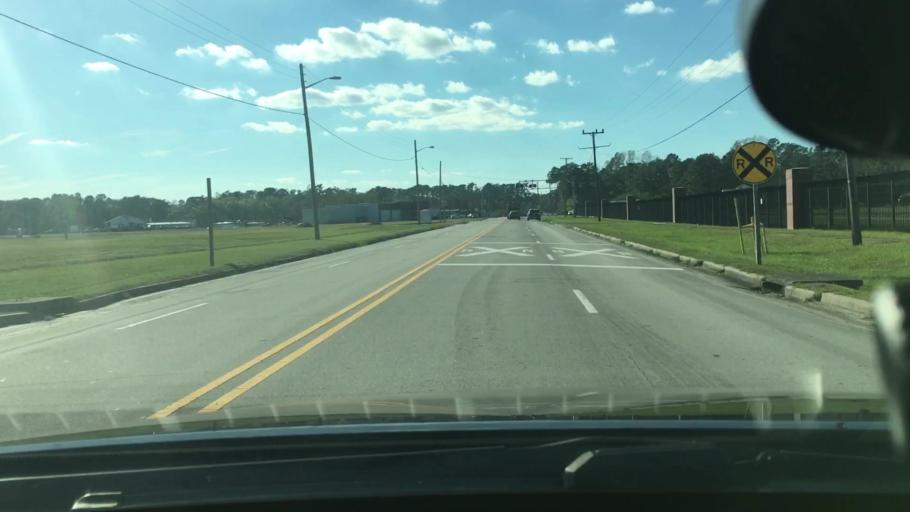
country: US
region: North Carolina
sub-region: Craven County
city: Havelock
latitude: 34.8826
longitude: -76.9024
